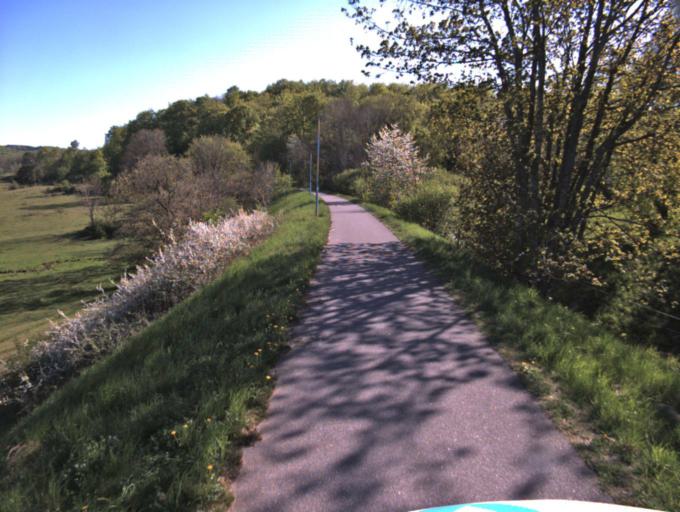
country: SE
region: Skane
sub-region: Kristianstads Kommun
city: Degeberga
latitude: 55.8368
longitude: 14.0788
